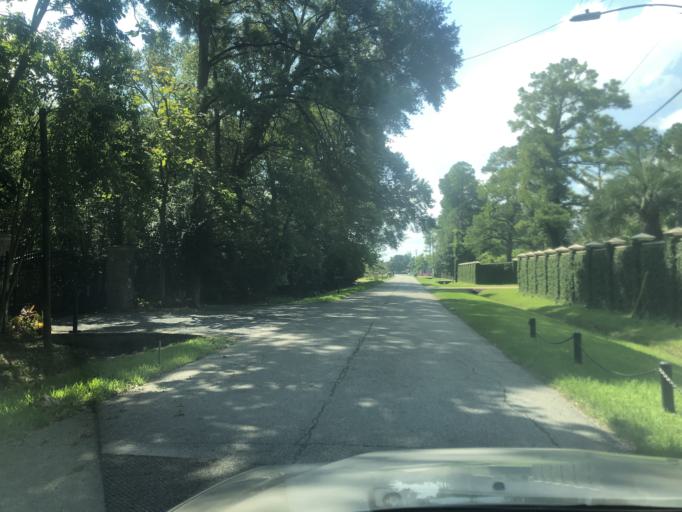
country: US
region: Texas
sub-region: Harris County
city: Bunker Hill Village
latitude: 29.7401
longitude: -95.5457
